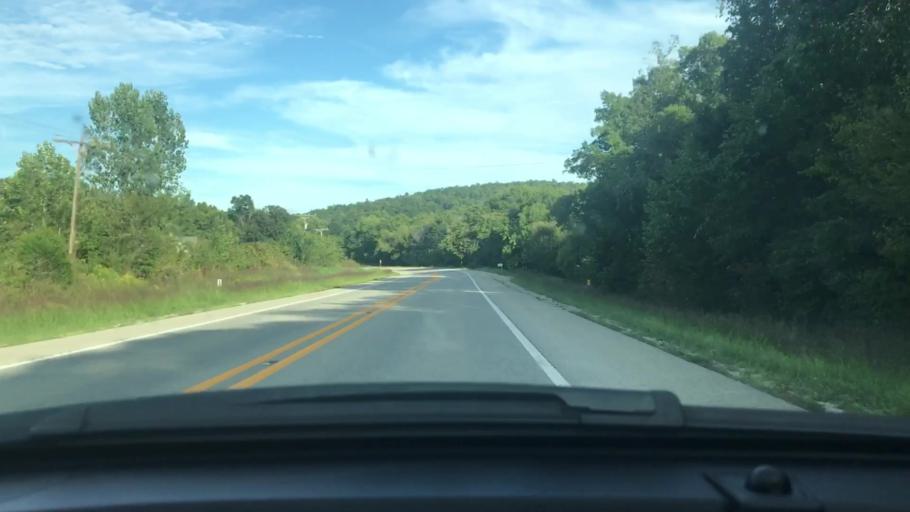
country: US
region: Arkansas
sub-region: Sharp County
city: Cherokee Village
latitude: 36.2736
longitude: -91.3367
